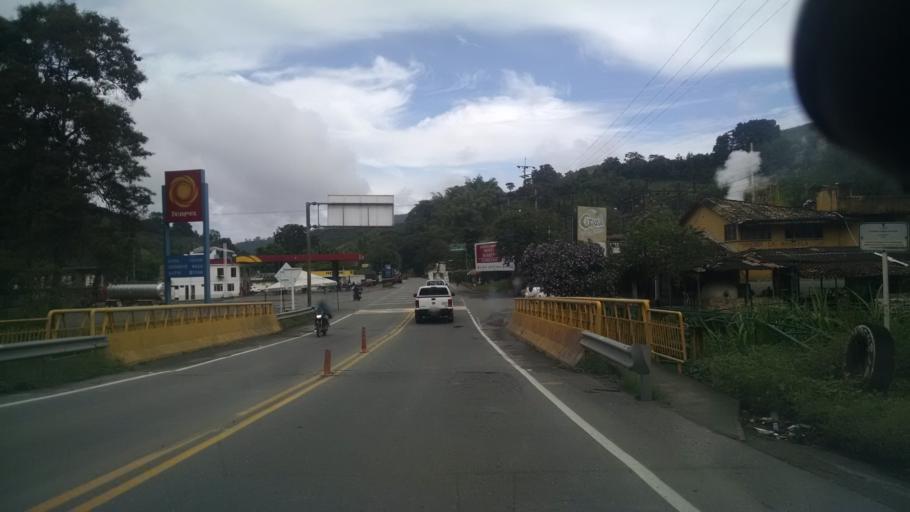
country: CO
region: Caldas
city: Palestina
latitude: 5.0585
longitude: -75.6073
